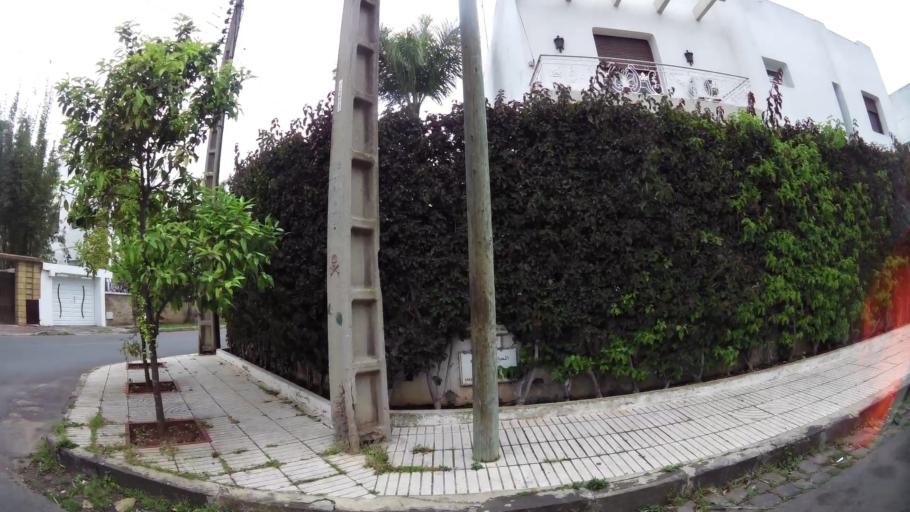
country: MA
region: Grand Casablanca
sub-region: Casablanca
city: Casablanca
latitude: 33.5643
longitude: -7.6158
